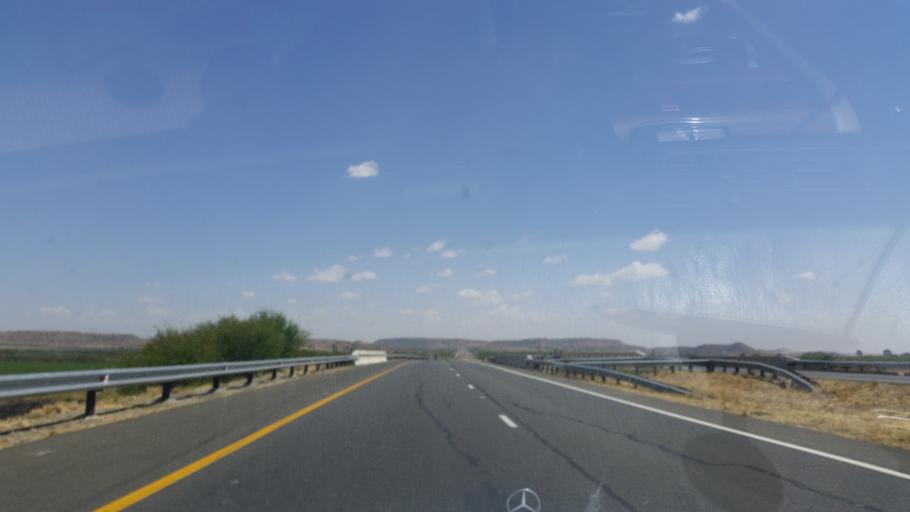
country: ZA
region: Orange Free State
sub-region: Mangaung Metropolitan Municipality
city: Bloemfontein
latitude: -28.9653
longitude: 26.3475
